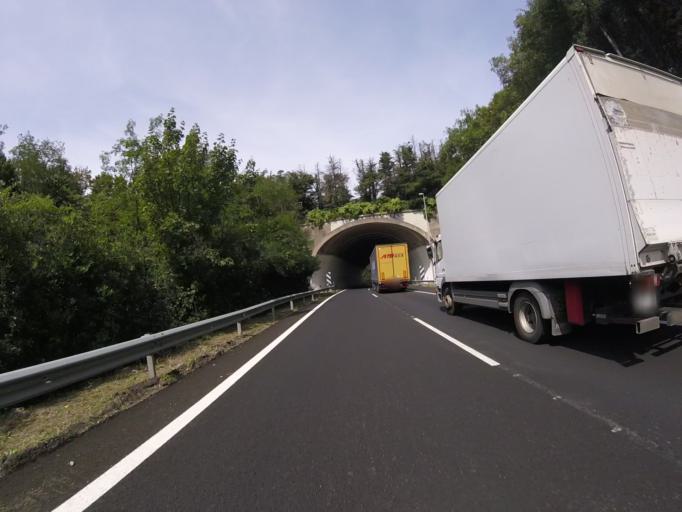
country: ES
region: Basque Country
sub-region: Provincia de Guipuzcoa
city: San Sebastian
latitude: 43.3024
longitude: -1.9692
